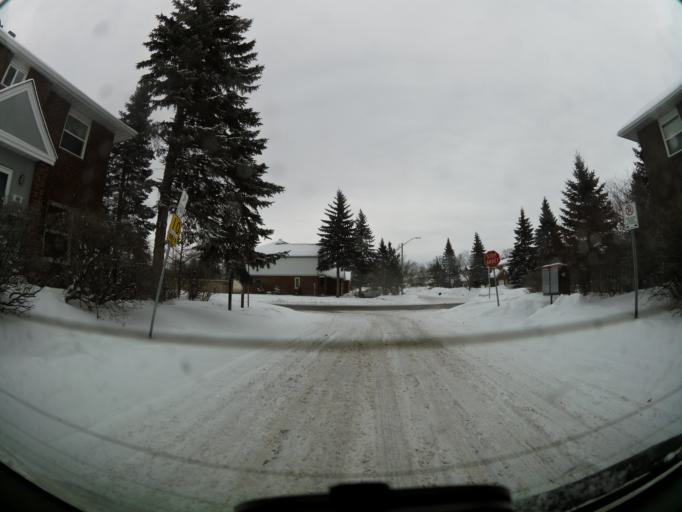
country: CA
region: Ontario
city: Ottawa
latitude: 45.3690
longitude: -75.6160
